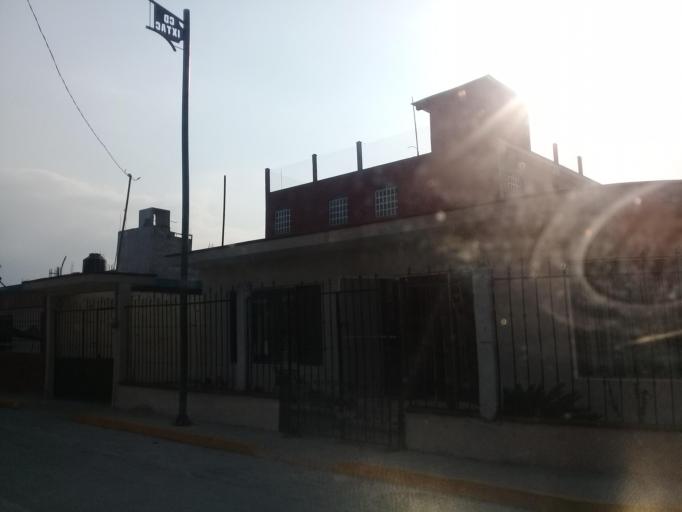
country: MX
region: Veracruz
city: Ixtac Zoquitlan
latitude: 18.8562
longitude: -97.0536
